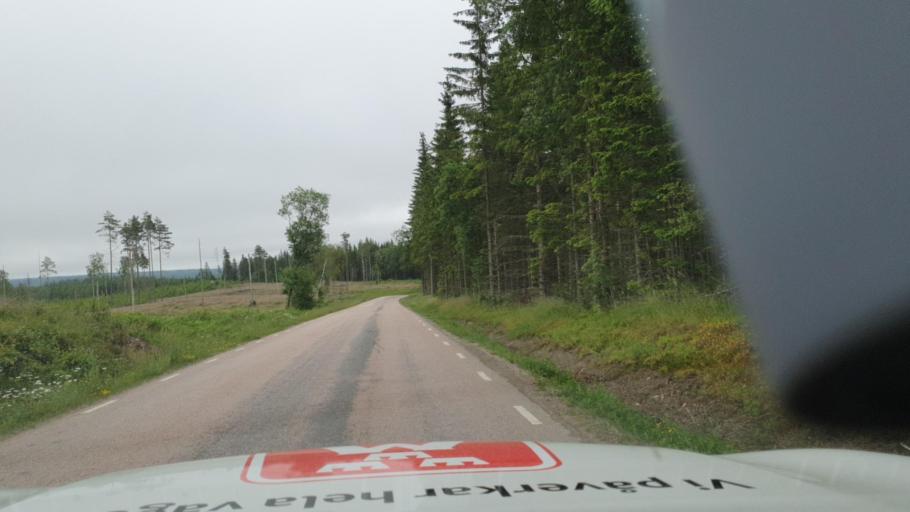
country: SE
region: Joenkoeping
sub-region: Mullsjo Kommun
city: Mullsjoe
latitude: 57.8803
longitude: 13.7266
